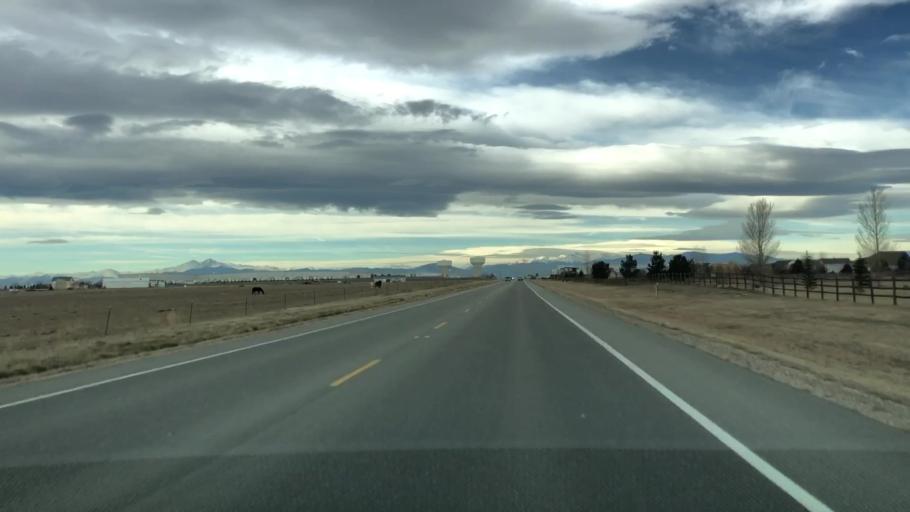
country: US
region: Colorado
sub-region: Weld County
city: Windsor
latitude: 40.4360
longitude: -104.9558
